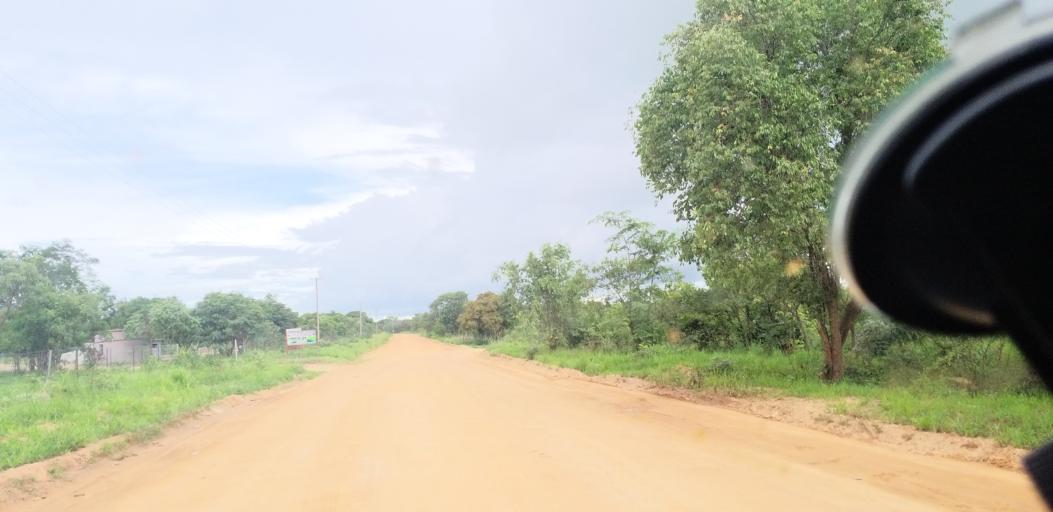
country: ZM
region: Lusaka
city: Chongwe
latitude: -15.1789
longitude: 28.4555
